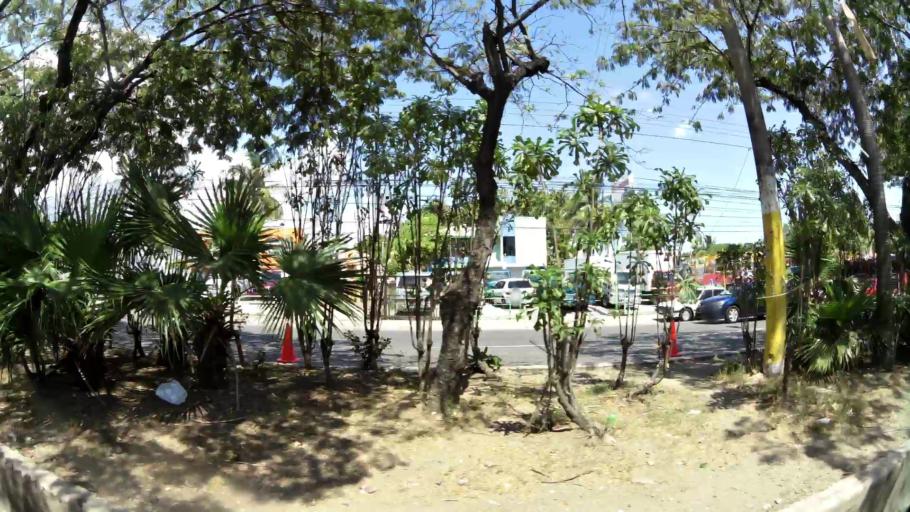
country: DO
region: Nacional
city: Santo Domingo
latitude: 18.4637
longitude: -69.9935
